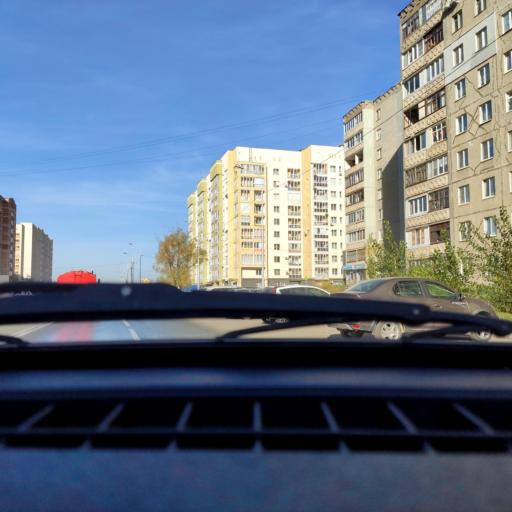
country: RU
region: Bashkortostan
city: Ufa
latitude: 54.7826
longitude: 56.1156
